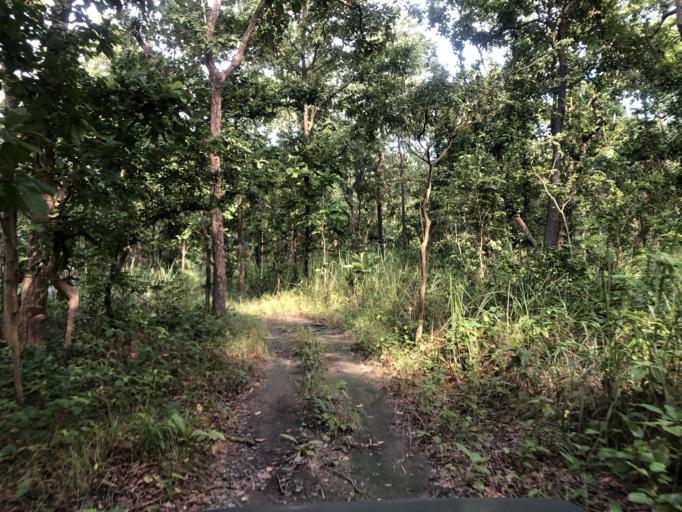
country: NP
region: Far Western
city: Tikapur
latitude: 28.5521
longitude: 81.2780
